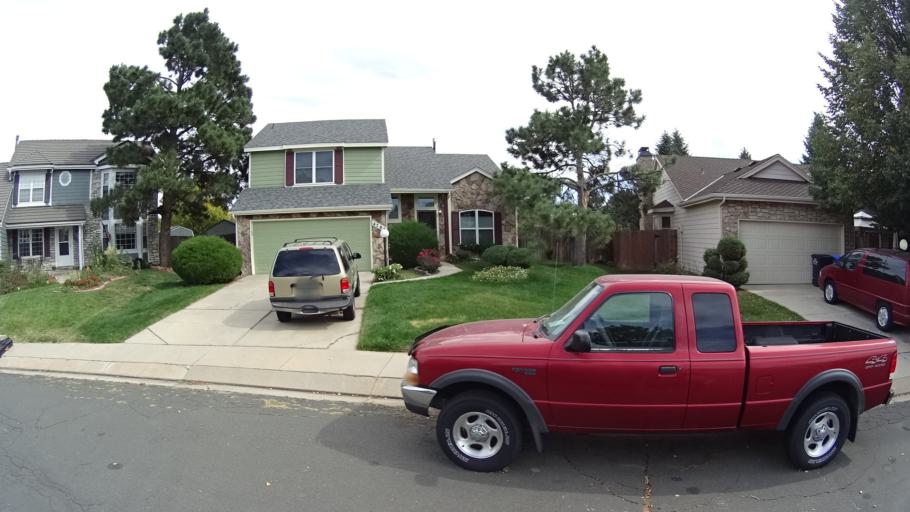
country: US
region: Colorado
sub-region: El Paso County
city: Cimarron Hills
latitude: 38.9007
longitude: -104.7031
